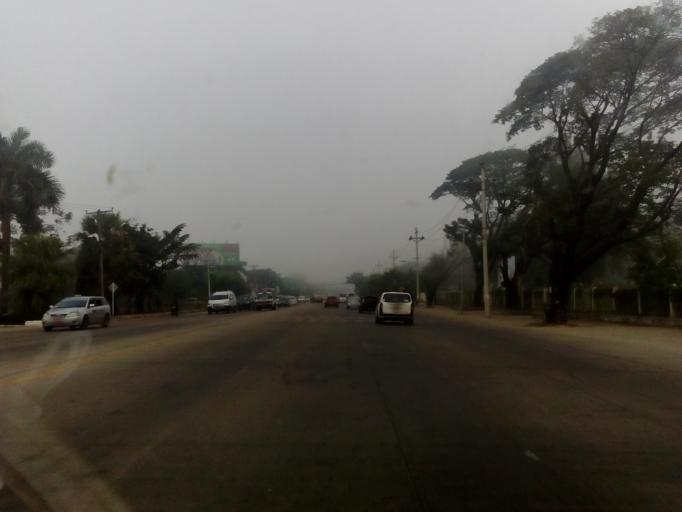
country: MM
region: Yangon
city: Yangon
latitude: 16.8184
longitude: 96.1869
